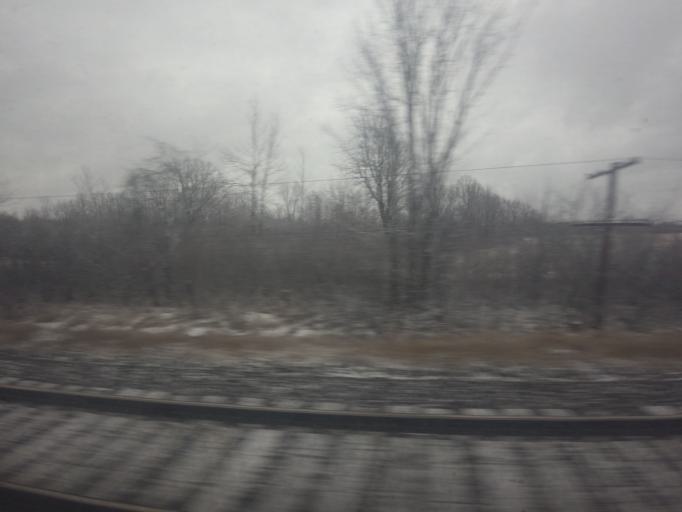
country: US
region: New York
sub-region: Jefferson County
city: Alexandria Bay
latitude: 44.4114
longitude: -76.0043
